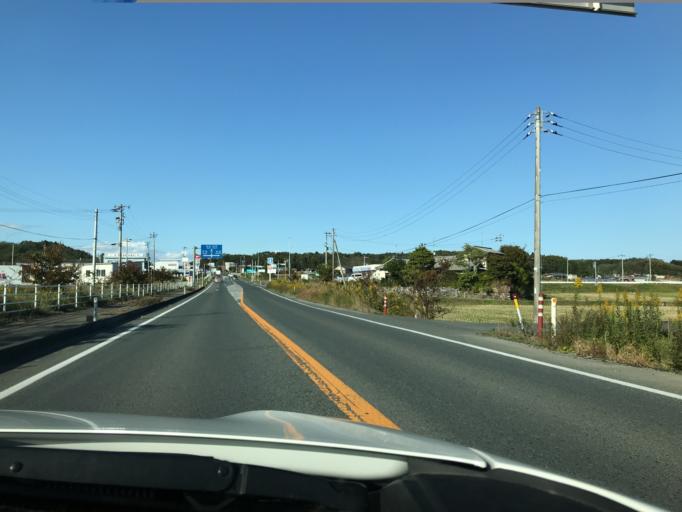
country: JP
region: Miyagi
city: Marumori
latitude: 37.7683
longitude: 140.9441
